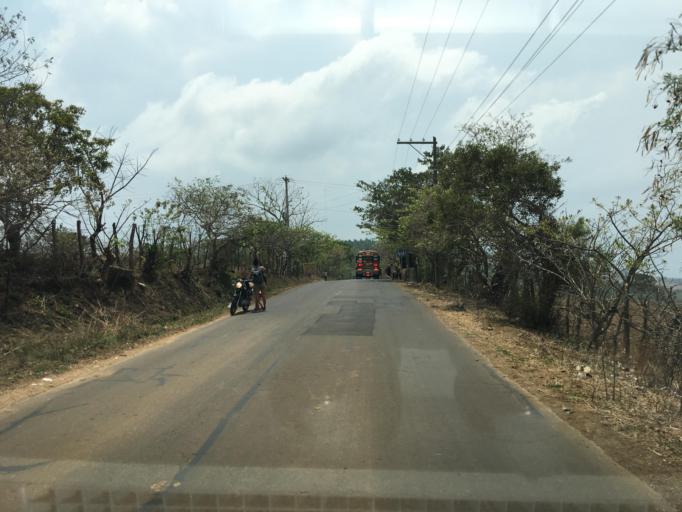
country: GT
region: Santa Rosa
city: Pueblo Nuevo Vinas
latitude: 14.3182
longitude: -90.5565
